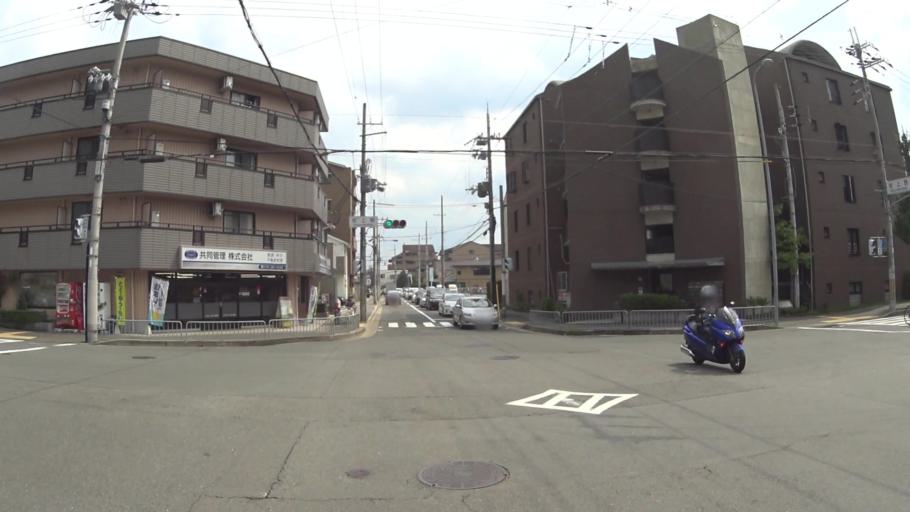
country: JP
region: Kyoto
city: Muko
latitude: 34.9944
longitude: 135.7016
